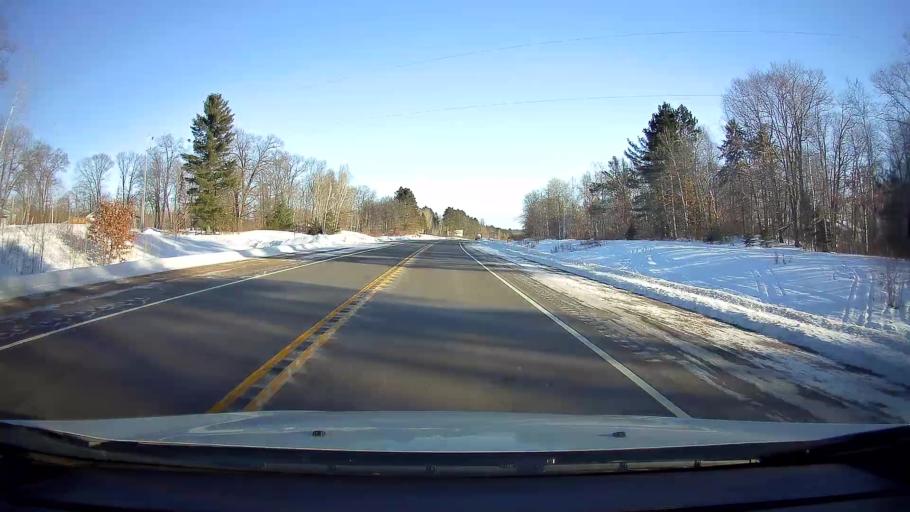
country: US
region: Wisconsin
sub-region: Sawyer County
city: Hayward
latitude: 46.0639
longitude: -91.4380
